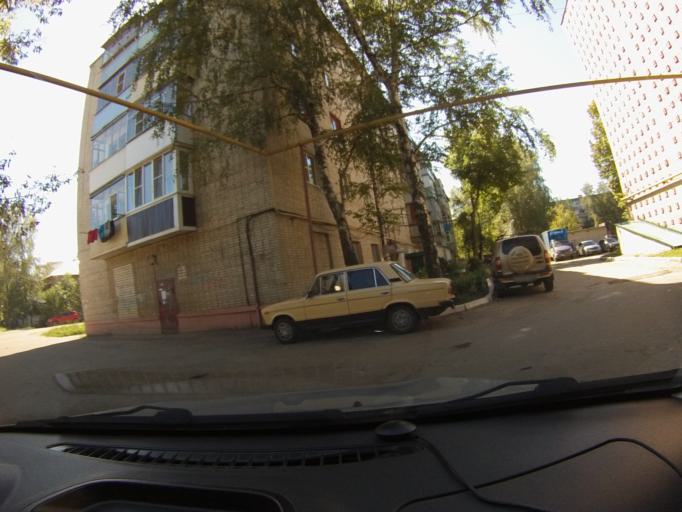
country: RU
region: Tambov
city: Donskoye
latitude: 52.7603
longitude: 41.4735
